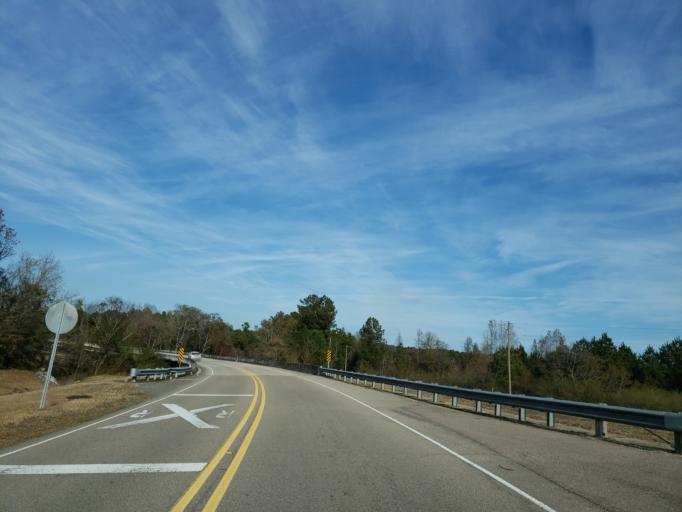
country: US
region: Mississippi
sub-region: Forrest County
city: Rawls Springs
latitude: 31.3949
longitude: -89.3658
